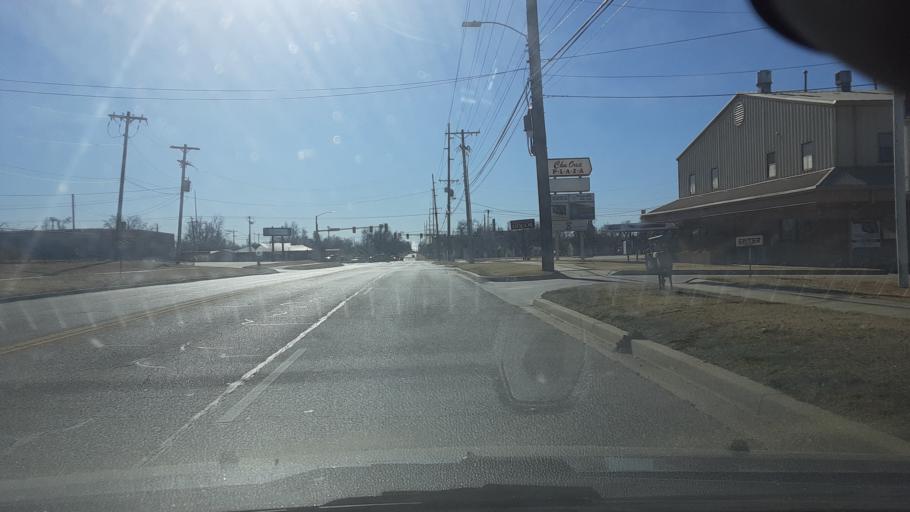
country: US
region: Oklahoma
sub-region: Kay County
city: Ponca City
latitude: 36.7259
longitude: -97.0852
